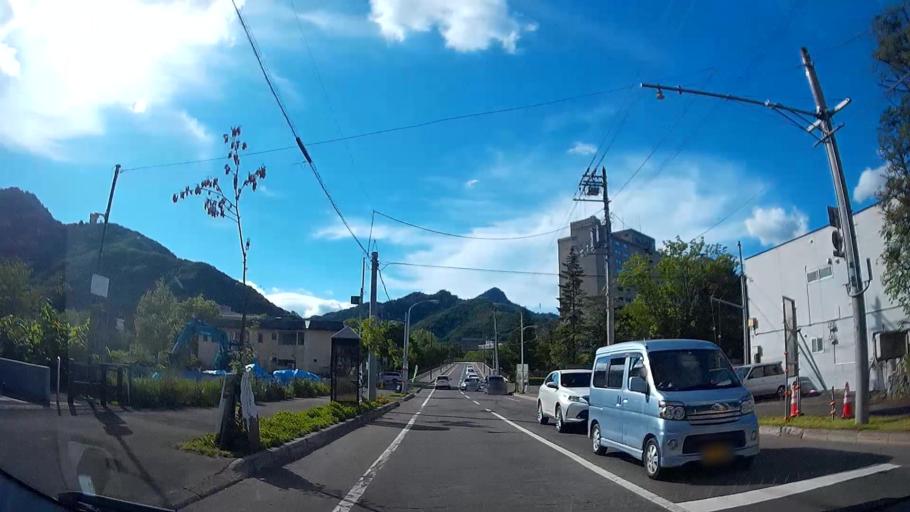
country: JP
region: Hokkaido
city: Sapporo
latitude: 42.9673
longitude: 141.1680
